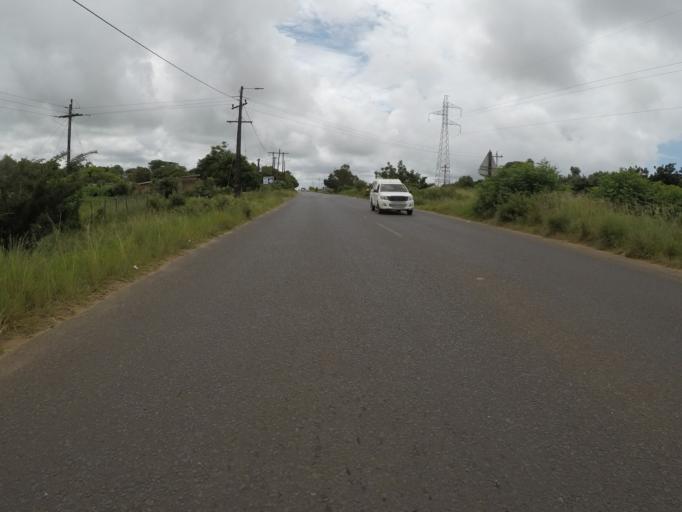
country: ZA
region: KwaZulu-Natal
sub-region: uThungulu District Municipality
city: eSikhawini
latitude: -28.8440
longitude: 31.9331
